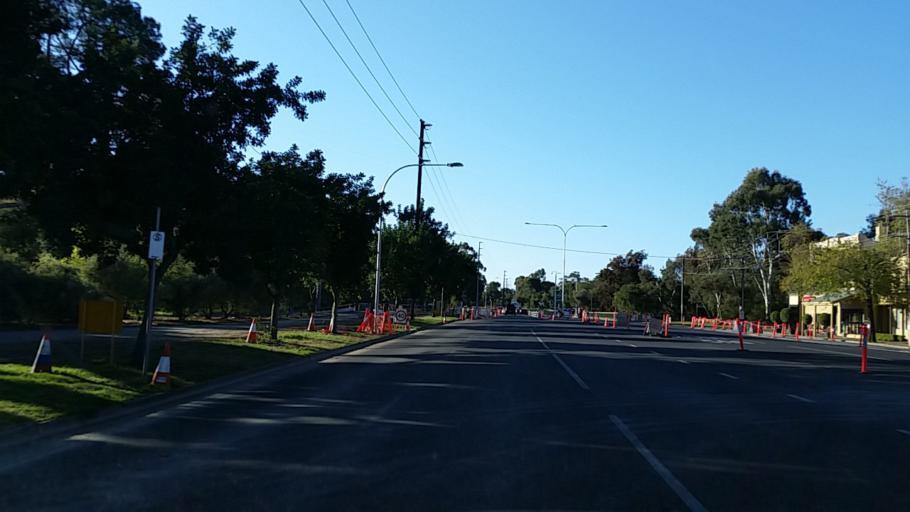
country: AU
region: South Australia
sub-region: Adelaide
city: North Adelaide
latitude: -34.9110
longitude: 138.6130
